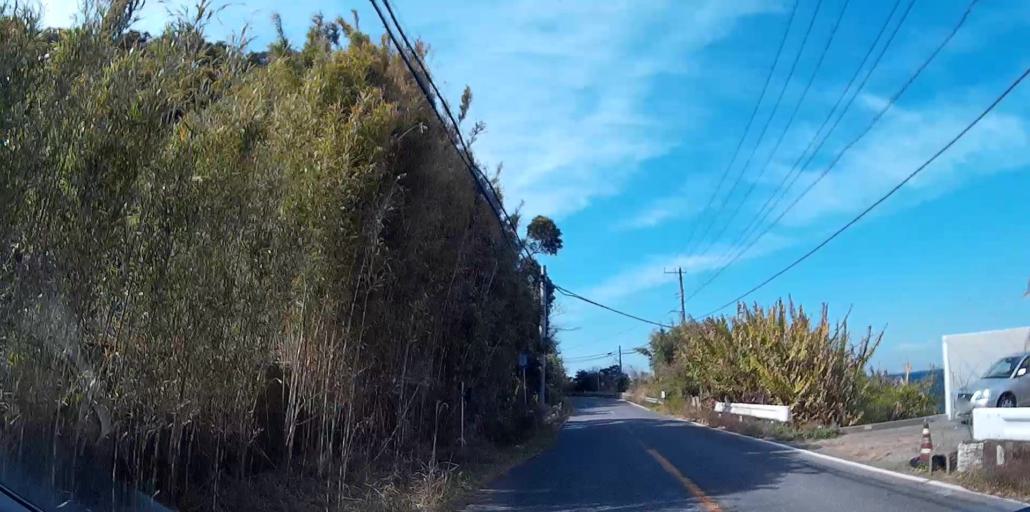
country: JP
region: Chiba
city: Tateyama
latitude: 34.9745
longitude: 139.7671
